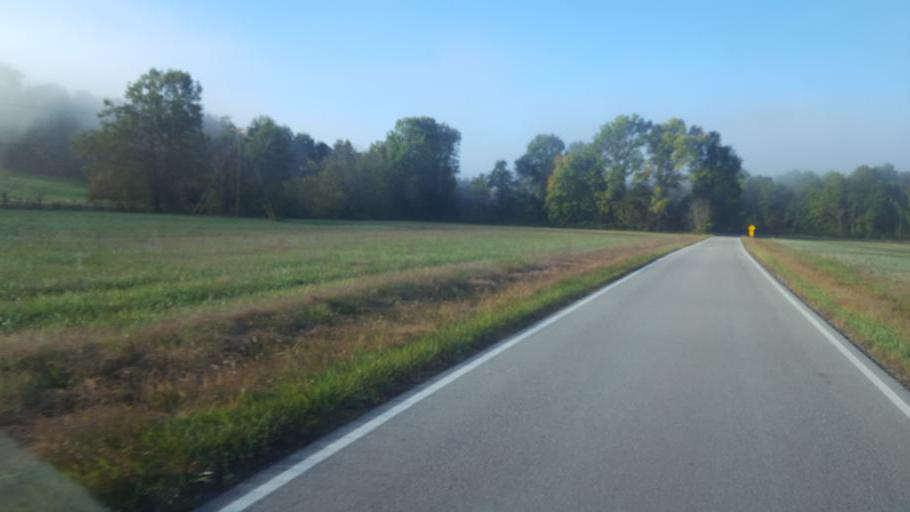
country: US
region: Ohio
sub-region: Adams County
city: Manchester
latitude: 38.5073
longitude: -83.5443
